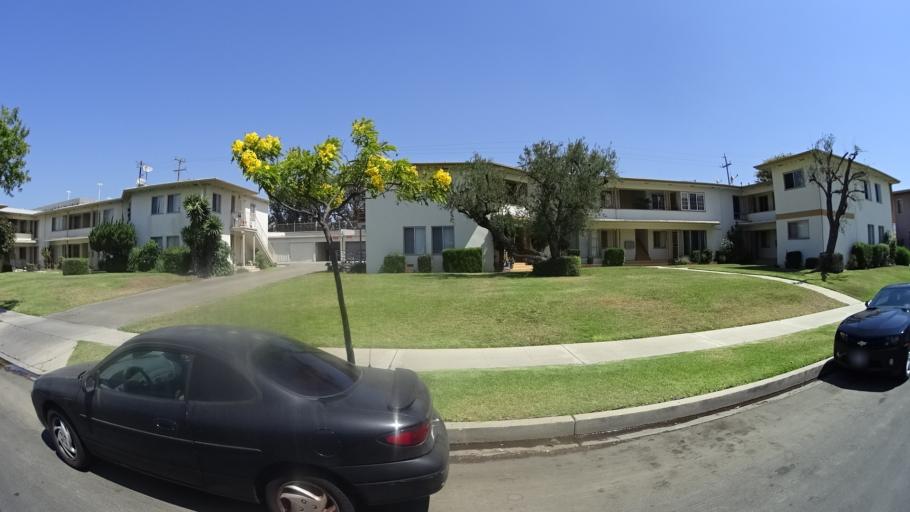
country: US
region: California
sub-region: Los Angeles County
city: Culver City
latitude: 34.0250
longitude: -118.3705
